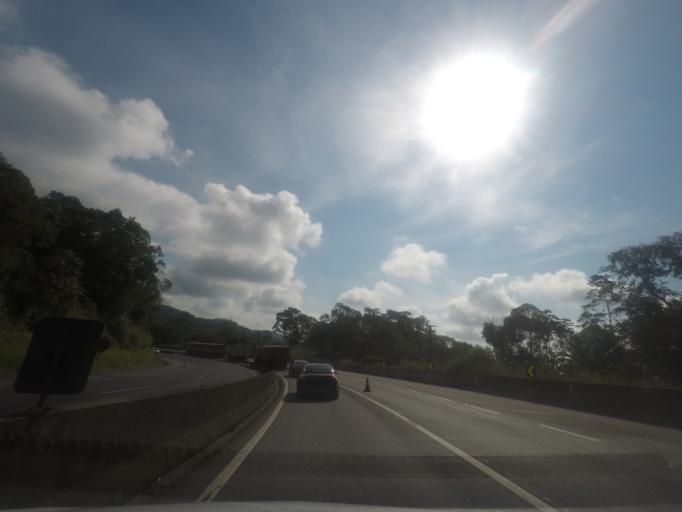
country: BR
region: Parana
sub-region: Antonina
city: Antonina
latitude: -25.5672
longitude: -48.8110
